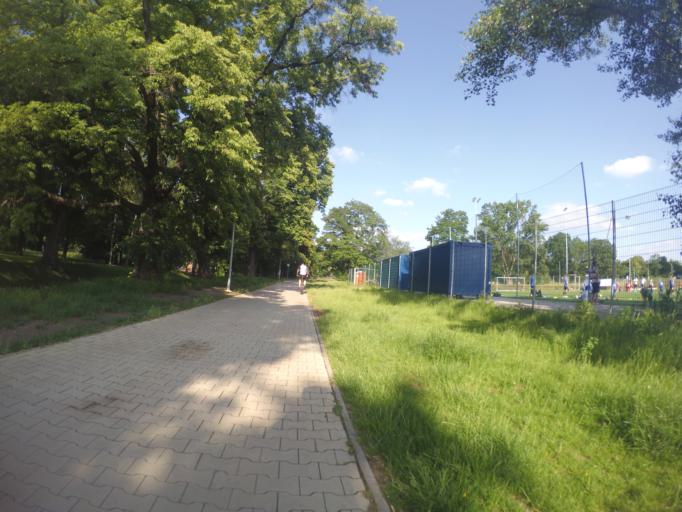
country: CZ
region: Praha
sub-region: Praha 9
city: Prosek
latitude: 50.1099
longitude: 14.4915
